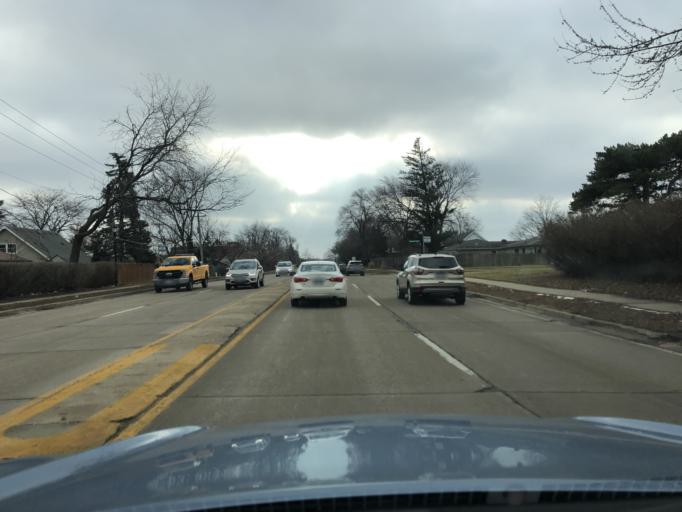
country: US
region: Illinois
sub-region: DuPage County
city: Itasca
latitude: 41.9991
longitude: -88.0035
